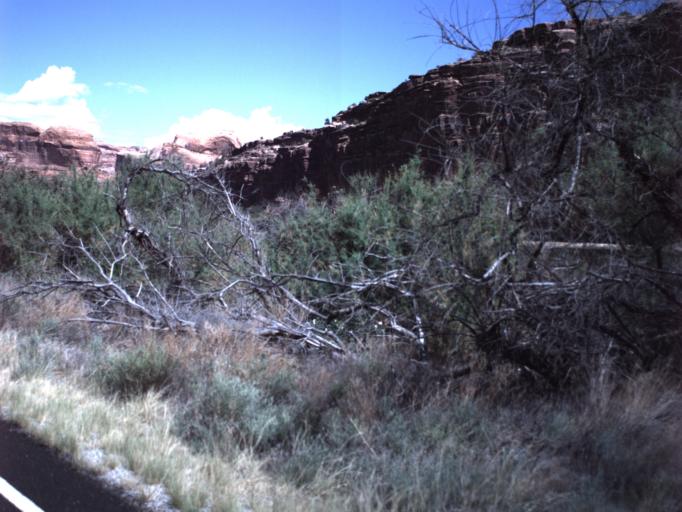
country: US
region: Utah
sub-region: Grand County
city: Moab
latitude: 38.5724
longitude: -109.6547
